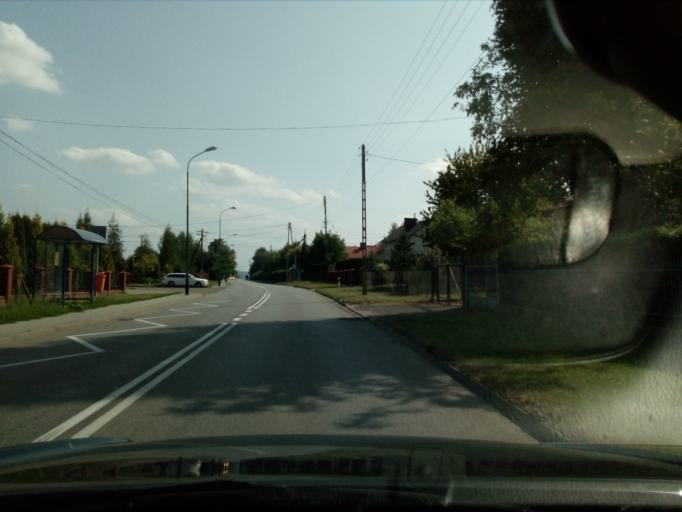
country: PL
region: Subcarpathian Voivodeship
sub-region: Powiat lancucki
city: Lancut
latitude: 50.0567
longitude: 22.2240
